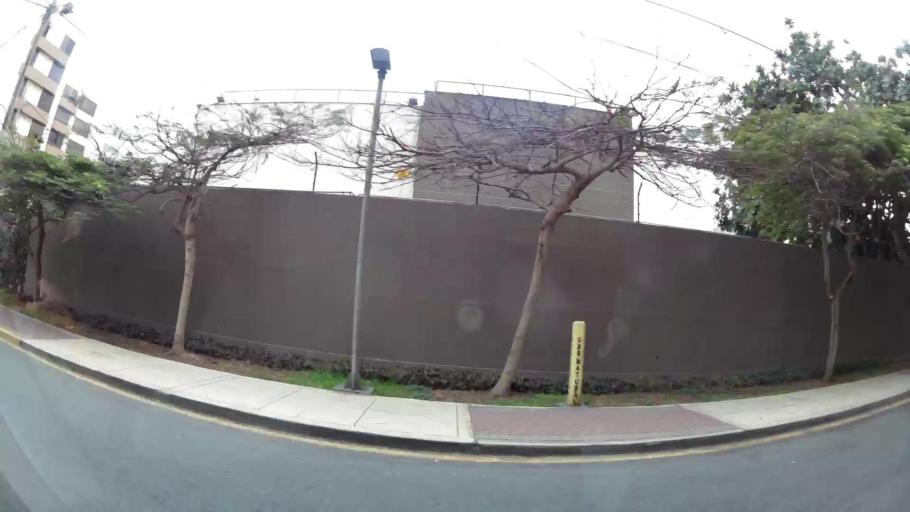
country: PE
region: Lima
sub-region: Lima
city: San Isidro
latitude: -12.0957
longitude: -77.0457
